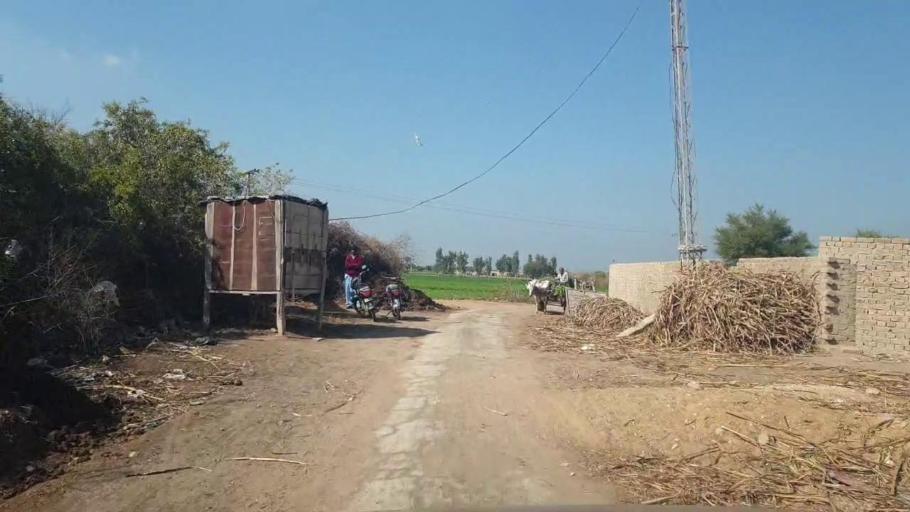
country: PK
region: Sindh
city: Shahdadpur
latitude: 25.9144
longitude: 68.5854
